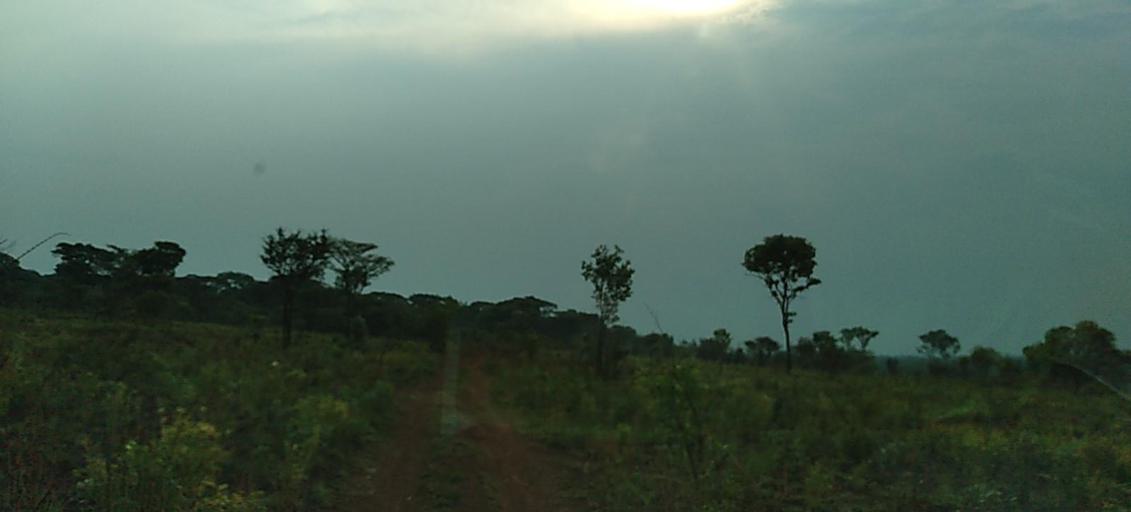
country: ZM
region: North-Western
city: Solwezi
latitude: -12.0434
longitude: 26.0263
